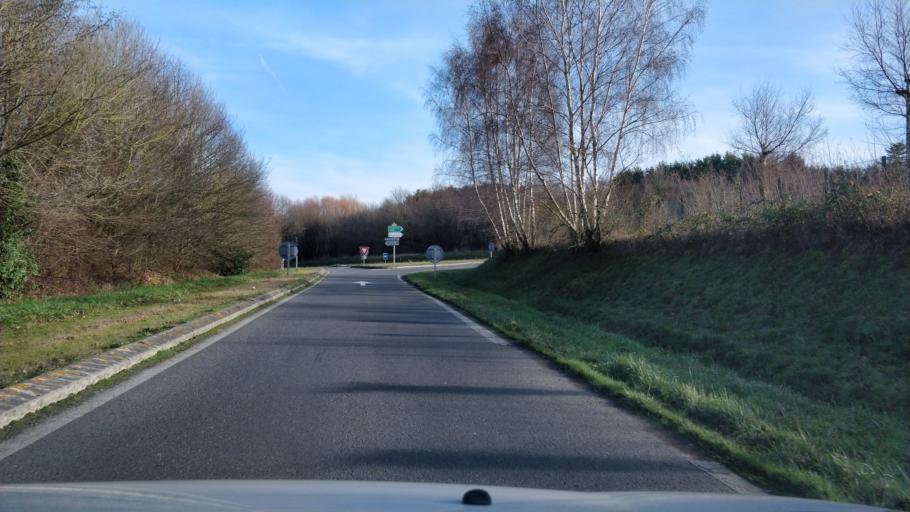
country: FR
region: Brittany
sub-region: Departement d'Ille-et-Vilaine
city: Dol-de-Bretagne
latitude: 48.5550
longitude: -1.7248
